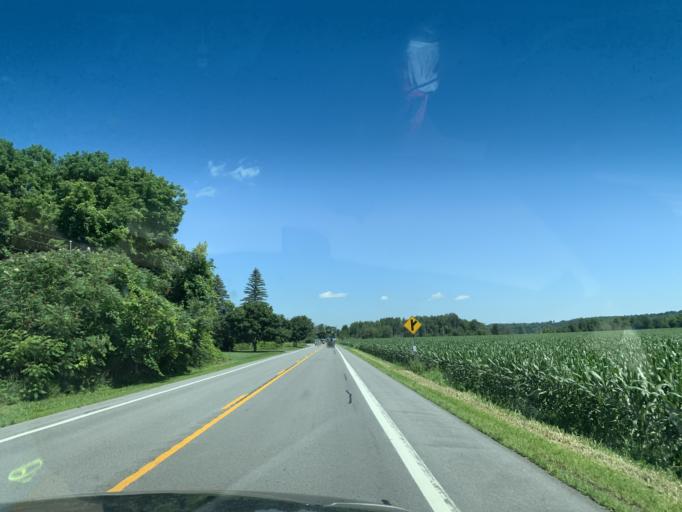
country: US
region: New York
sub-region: Oneida County
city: Chadwicks
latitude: 42.9079
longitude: -75.2407
